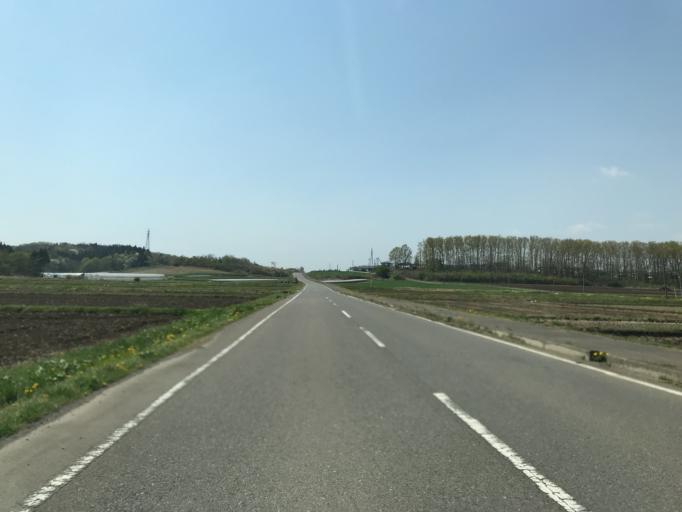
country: JP
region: Fukushima
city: Sukagawa
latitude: 37.1925
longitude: 140.3515
